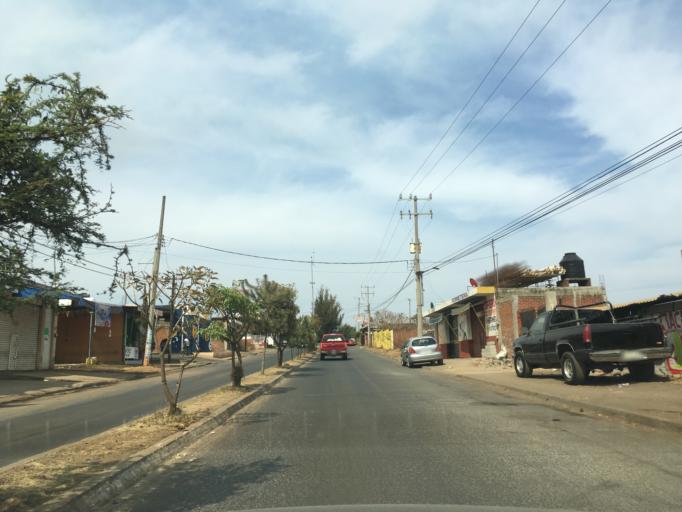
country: MX
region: Michoacan
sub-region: Uruapan
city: Uruapan
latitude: 19.3837
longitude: -102.0750
